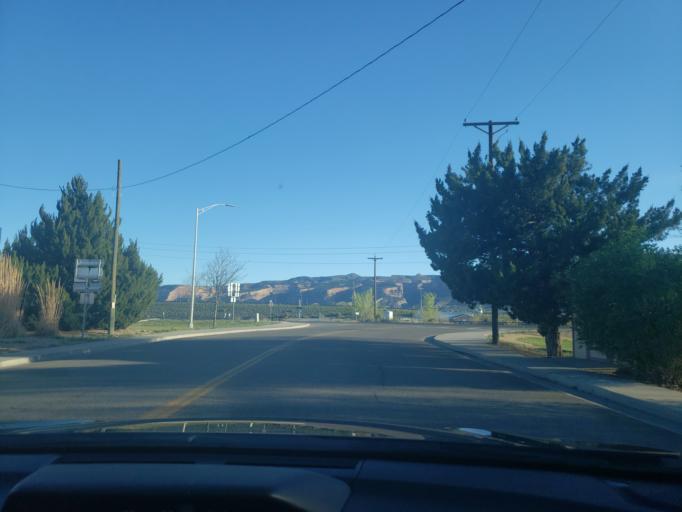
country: US
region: Colorado
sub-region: Mesa County
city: Fruita
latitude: 39.1587
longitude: -108.7383
